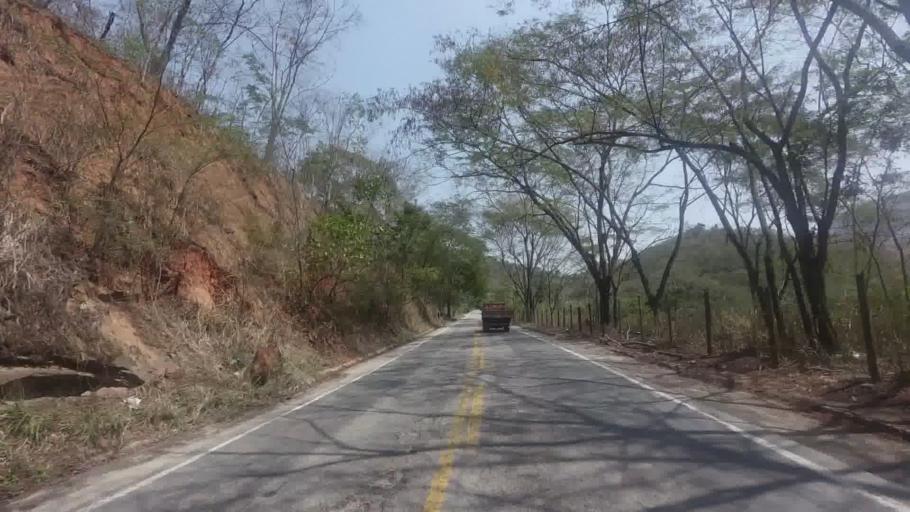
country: BR
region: Espirito Santo
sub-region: Cachoeiro De Itapemirim
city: Cachoeiro de Itapemirim
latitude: -20.8643
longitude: -41.0393
